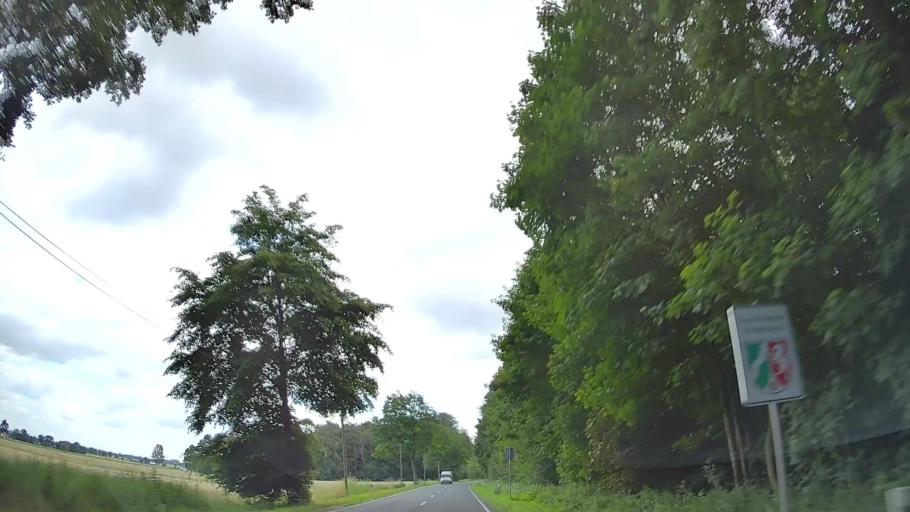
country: DE
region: Lower Saxony
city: Brockum
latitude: 52.4642
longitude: 8.4559
